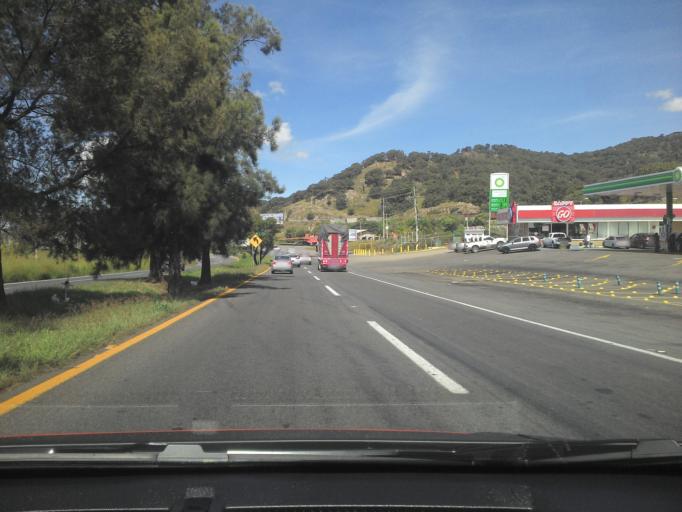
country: MX
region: Jalisco
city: La Venta del Astillero
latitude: 20.7336
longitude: -103.5776
